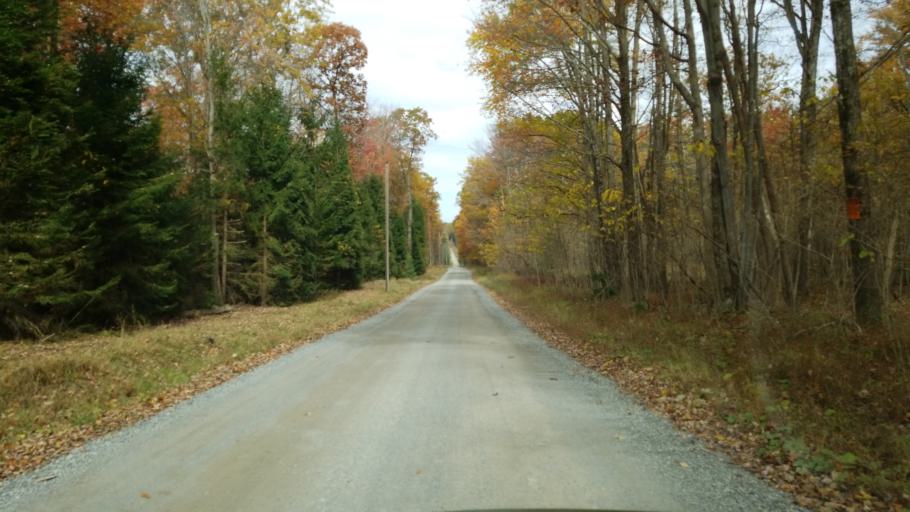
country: US
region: Pennsylvania
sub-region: Clearfield County
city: Clearfield
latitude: 41.1746
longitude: -78.4441
